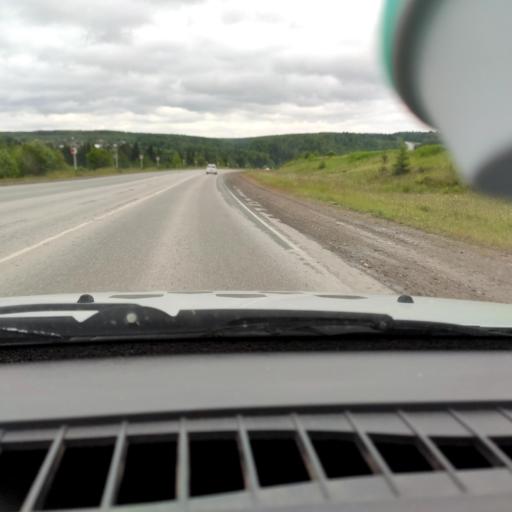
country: RU
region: Perm
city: Dobryanka
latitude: 58.4343
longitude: 56.5406
